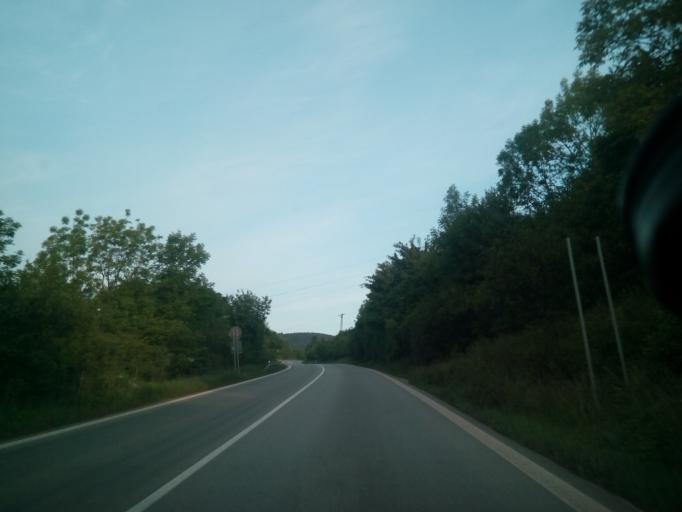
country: SK
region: Kosicky
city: Roznava
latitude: 48.5989
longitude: 20.6639
